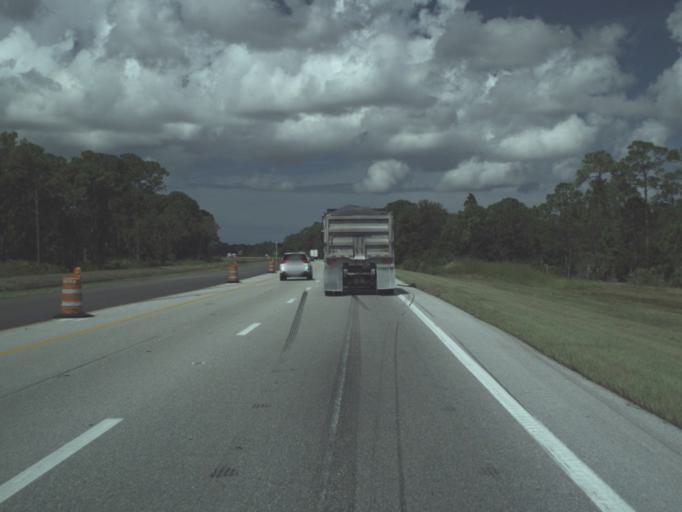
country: US
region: Florida
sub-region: Sarasota County
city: Warm Mineral Springs
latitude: 27.1108
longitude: -82.3113
